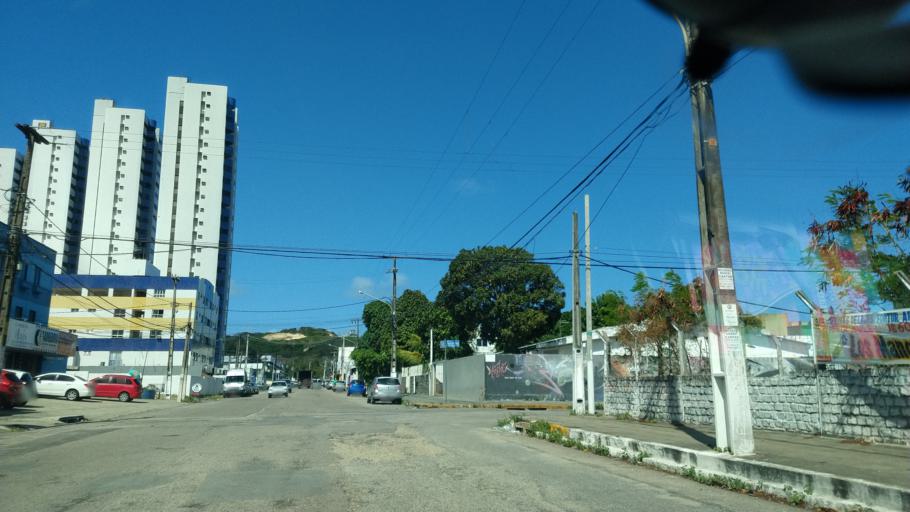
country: BR
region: Rio Grande do Norte
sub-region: Natal
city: Natal
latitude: -5.8689
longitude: -35.1868
